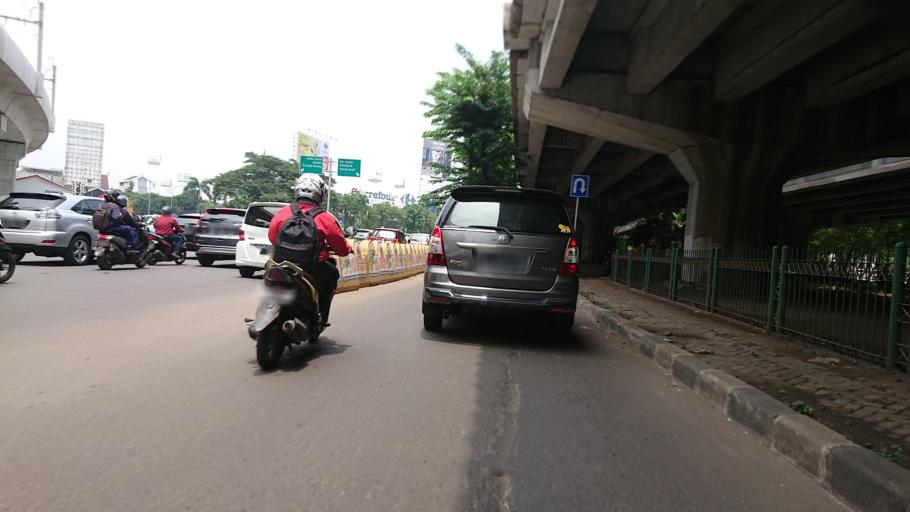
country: ID
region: Banten
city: South Tangerang
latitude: -6.2894
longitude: 106.7787
